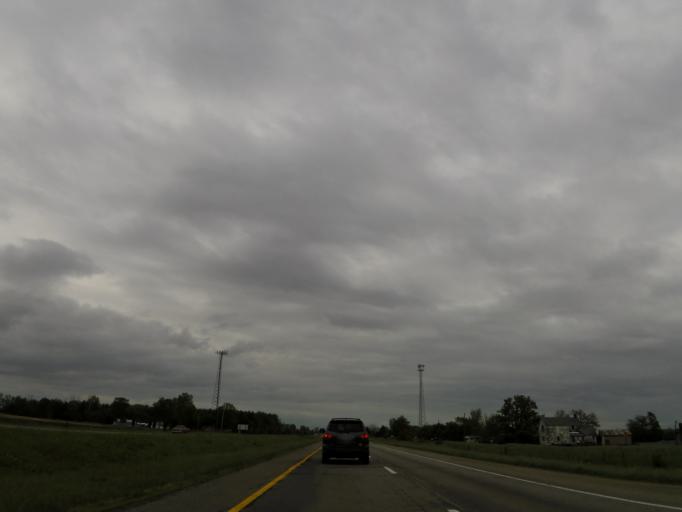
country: US
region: Ohio
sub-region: Madison County
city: Mount Sterling
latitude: 39.7797
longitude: -83.2591
